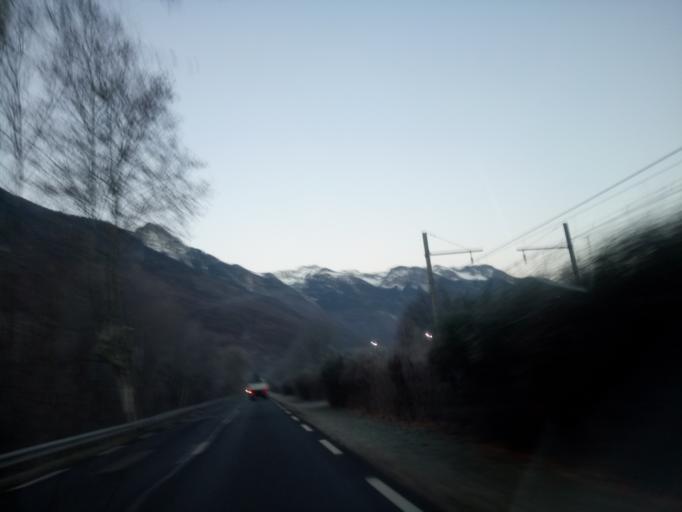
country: FR
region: Rhone-Alpes
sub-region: Departement de la Savoie
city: La Chambre
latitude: 45.3566
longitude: 6.2945
